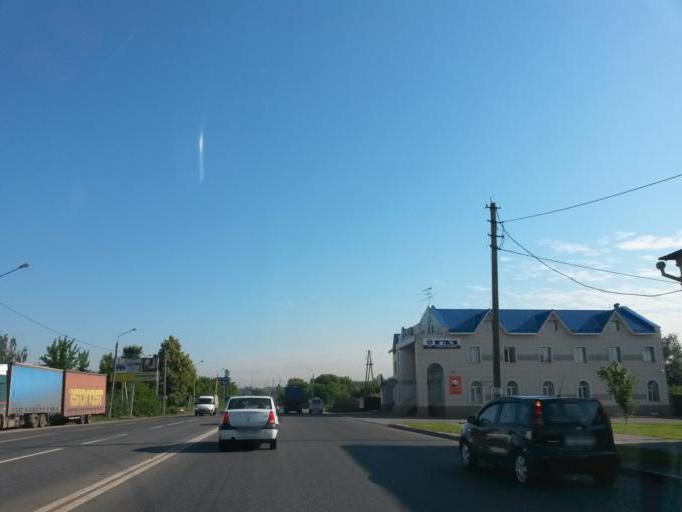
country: RU
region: Moskovskaya
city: Yam
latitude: 55.4894
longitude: 37.7502
